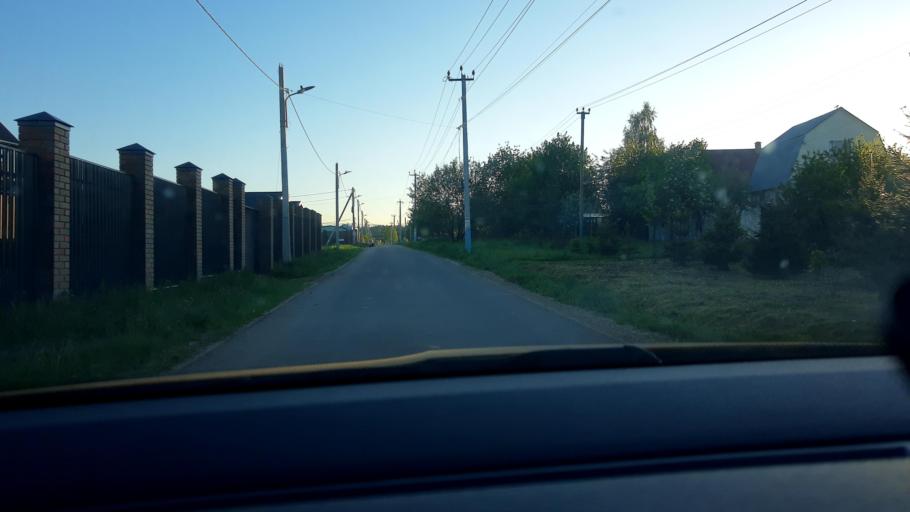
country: RU
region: Moskovskaya
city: Selyatino
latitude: 55.5030
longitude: 36.9250
